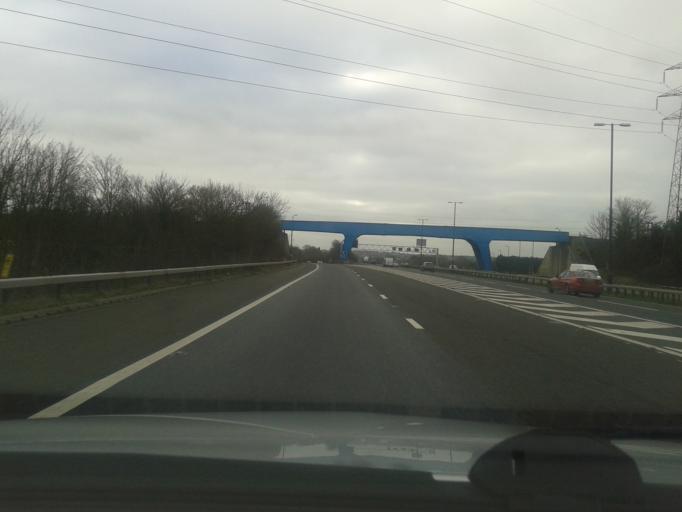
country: GB
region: England
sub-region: South Gloucestershire
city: Winterbourne
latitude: 51.5173
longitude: -2.5200
